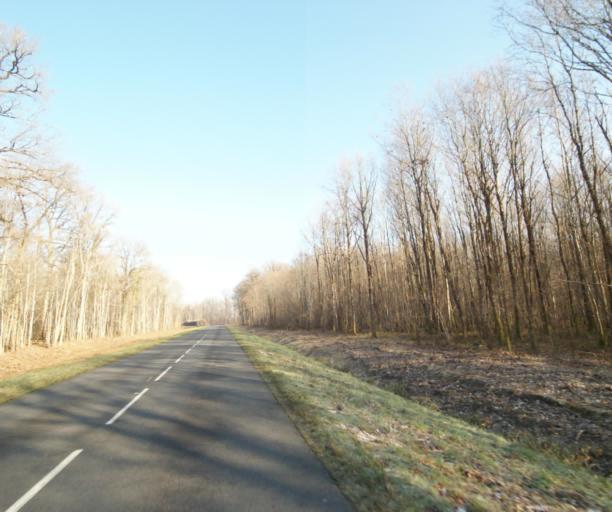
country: FR
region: Champagne-Ardenne
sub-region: Departement de la Haute-Marne
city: Wassy
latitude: 48.4794
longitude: 4.9321
